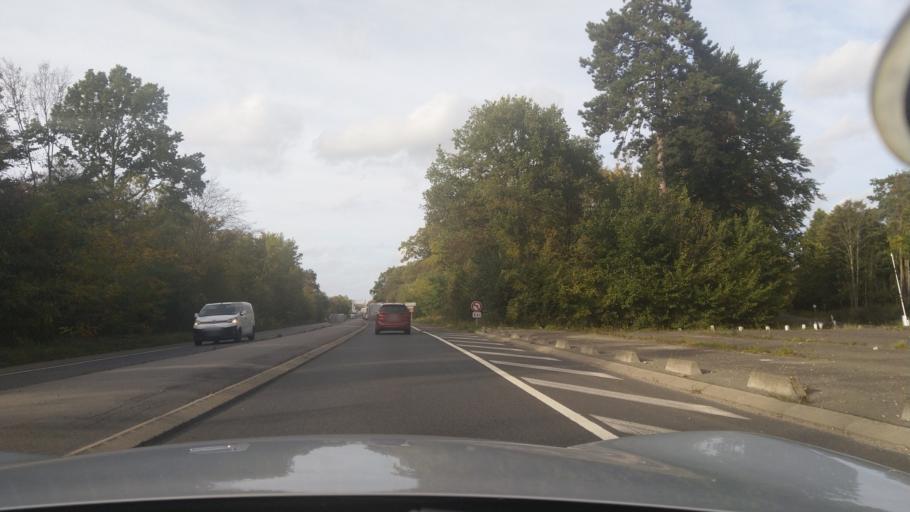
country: FR
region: Ile-de-France
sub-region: Departement des Yvelines
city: Acheres
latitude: 48.9502
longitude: 2.0943
